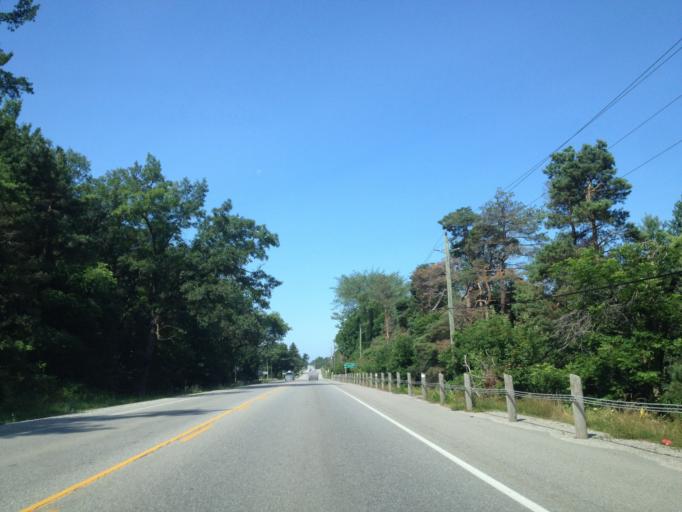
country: CA
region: Ontario
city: Norfolk County
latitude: 42.8376
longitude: -80.3523
